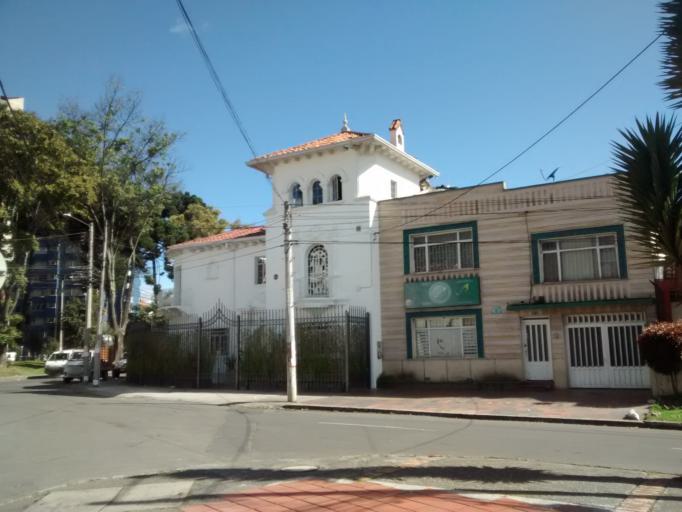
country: CO
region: Bogota D.C.
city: Bogota
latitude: 4.6199
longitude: -74.0719
